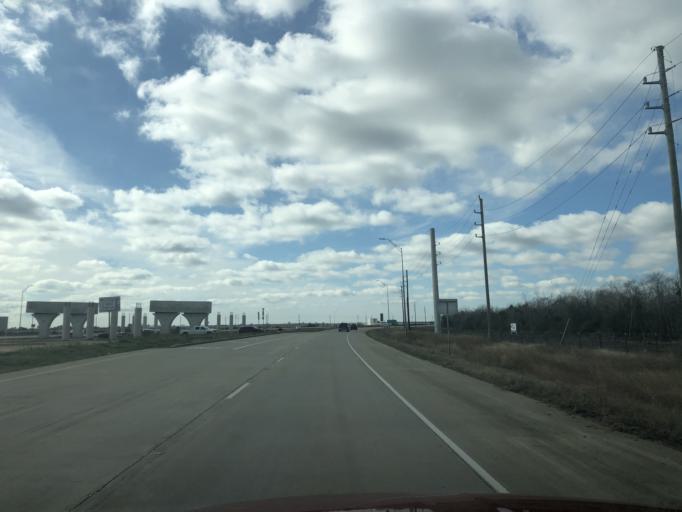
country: US
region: Texas
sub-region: Chambers County
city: Beach City
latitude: 29.7334
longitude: -94.8760
